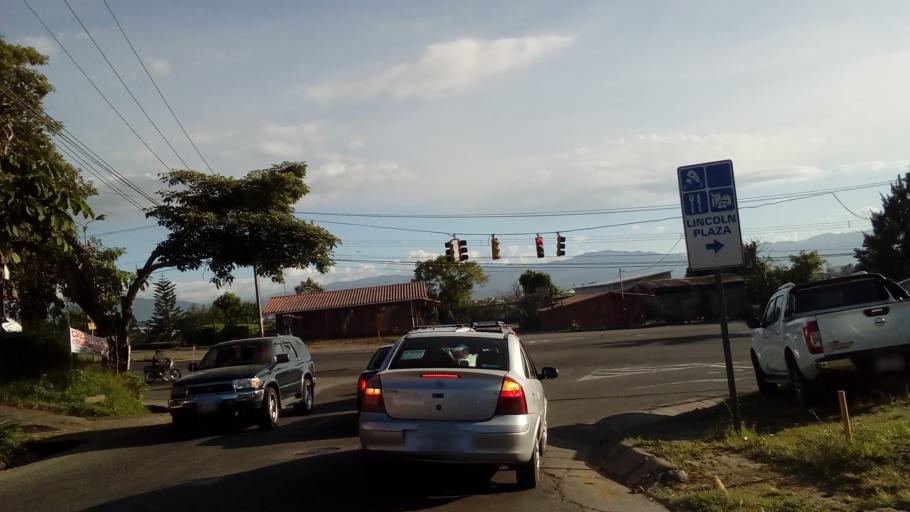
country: CR
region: Heredia
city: Angeles
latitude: 9.9796
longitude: -84.0533
